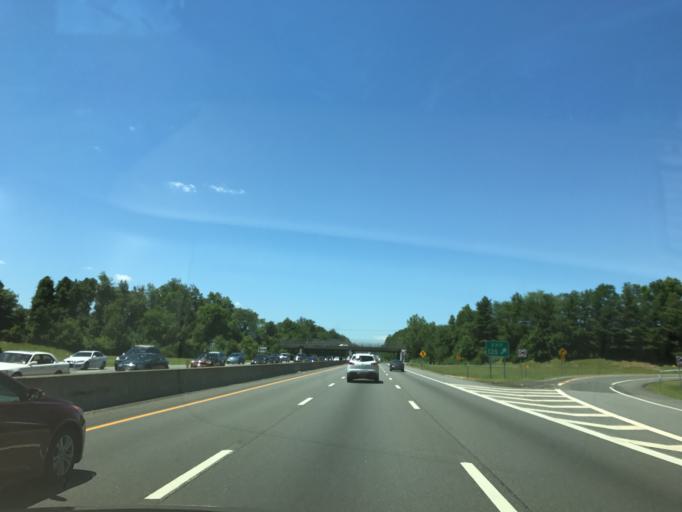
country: US
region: New York
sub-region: Rockland County
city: Bardonia
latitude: 41.1021
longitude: -73.9943
